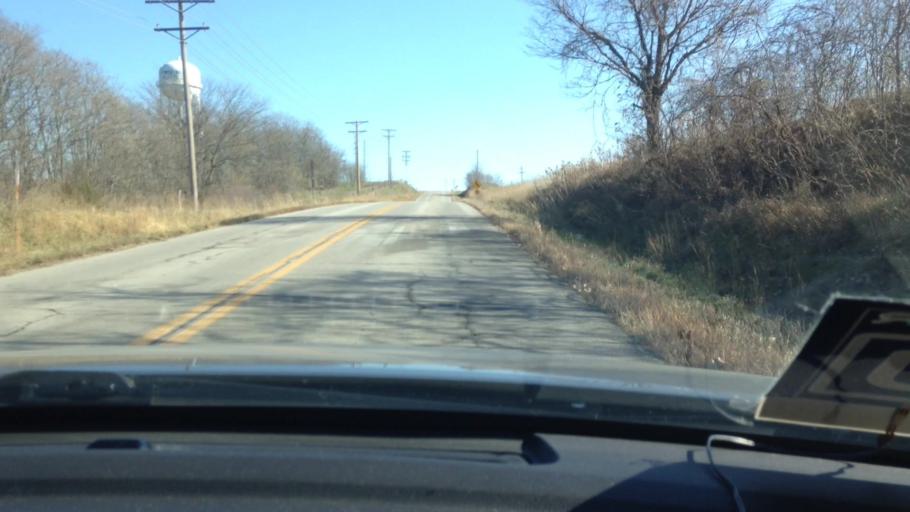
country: US
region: Missouri
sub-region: Platte County
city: Weston
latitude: 39.4828
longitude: -94.8956
